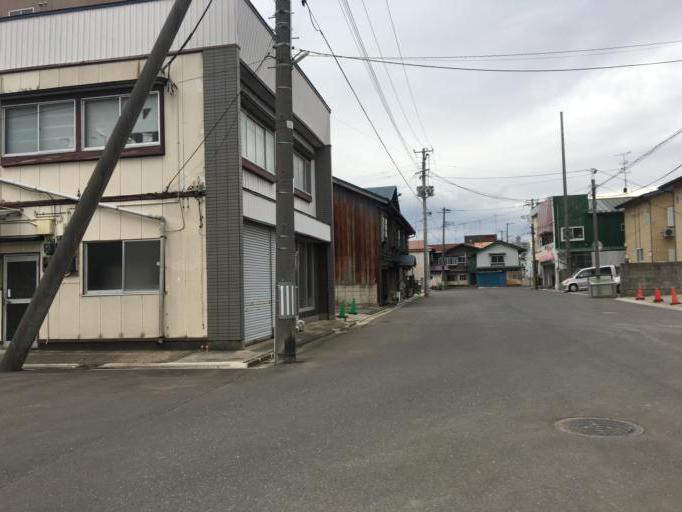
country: JP
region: Aomori
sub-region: Hachinohe Shi
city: Uchimaru
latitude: 40.5221
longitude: 141.5200
